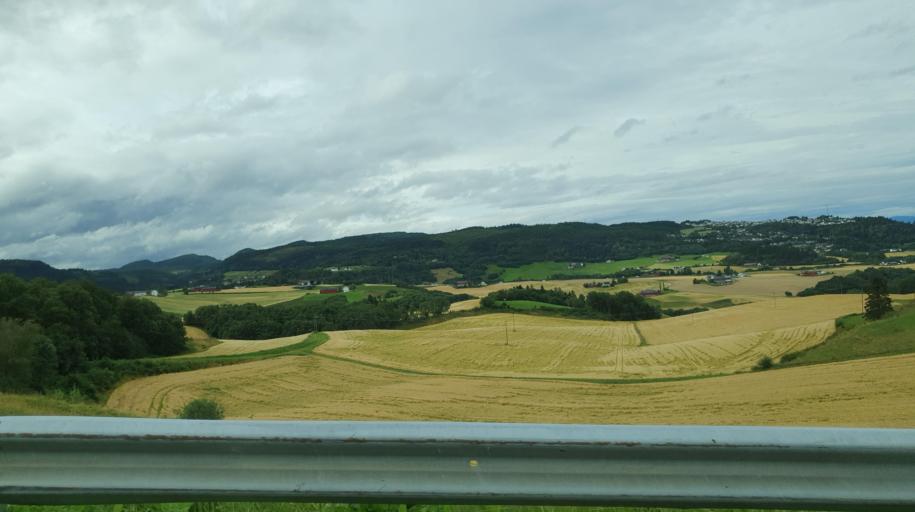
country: NO
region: Nord-Trondelag
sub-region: Stjordal
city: Stjordalshalsen
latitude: 63.4260
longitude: 10.9585
